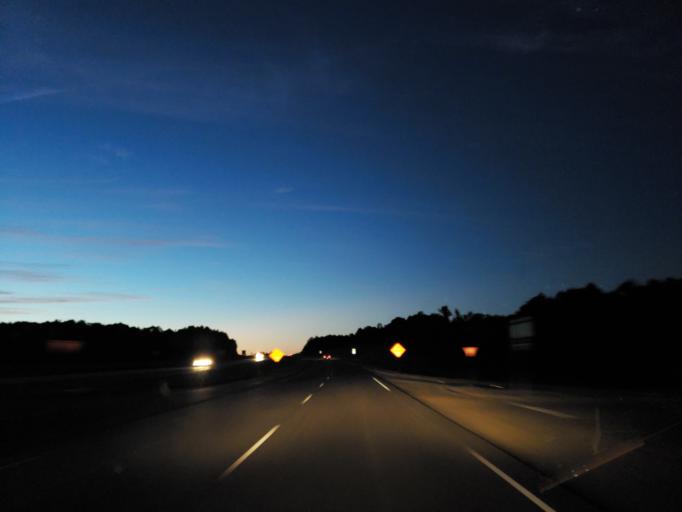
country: US
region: Mississippi
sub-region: Clarke County
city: Quitman
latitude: 32.1013
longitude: -88.7067
